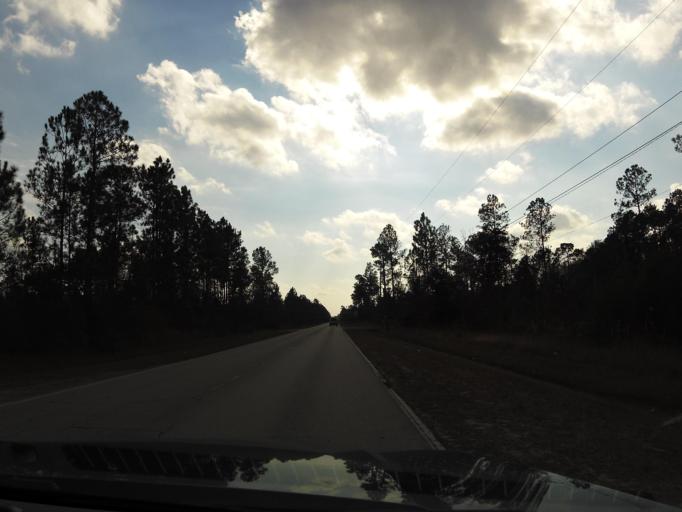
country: US
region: Florida
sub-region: Duval County
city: Baldwin
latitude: 30.2023
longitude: -81.9913
